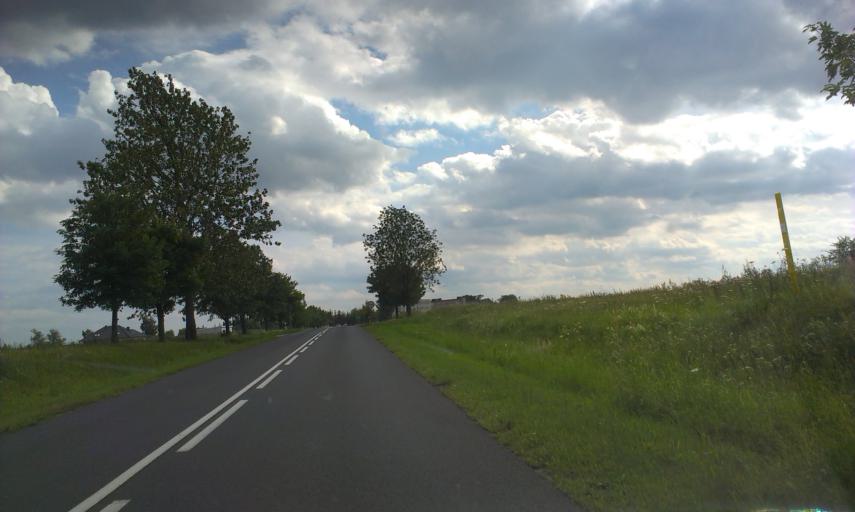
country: PL
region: Greater Poland Voivodeship
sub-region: Powiat zlotowski
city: Zlotow
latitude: 53.3379
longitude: 17.0133
